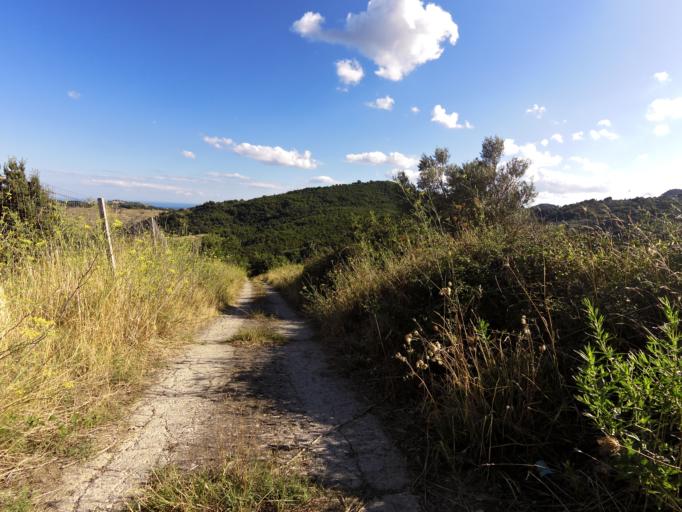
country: IT
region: Calabria
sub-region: Provincia di Reggio Calabria
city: Pazzano
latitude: 38.4451
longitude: 16.4493
